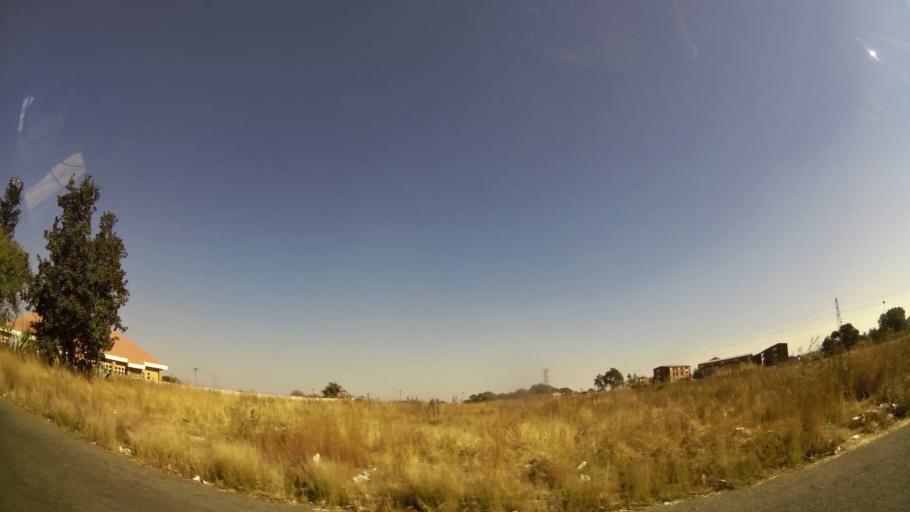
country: ZA
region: Gauteng
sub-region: City of Johannesburg Metropolitan Municipality
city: Roodepoort
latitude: -26.1791
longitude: 27.9543
